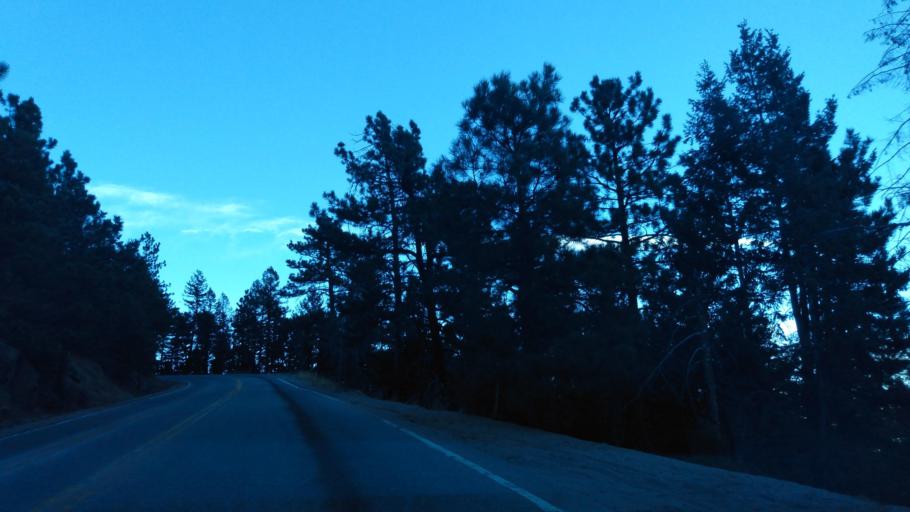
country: US
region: Colorado
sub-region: Boulder County
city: Coal Creek
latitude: 39.9843
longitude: -105.3748
